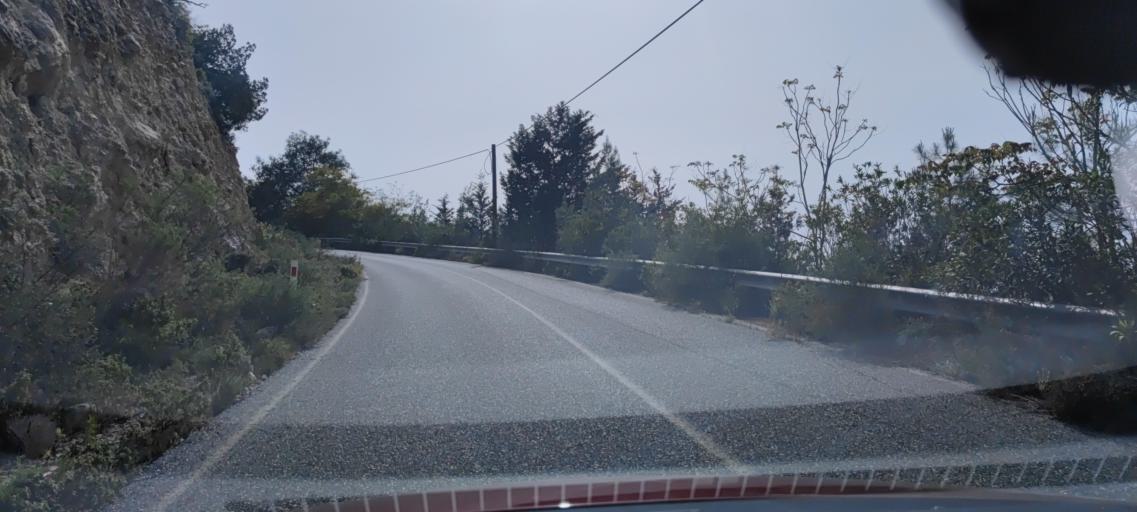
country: CY
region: Ammochostos
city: Trikomo
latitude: 35.3983
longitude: 33.9001
